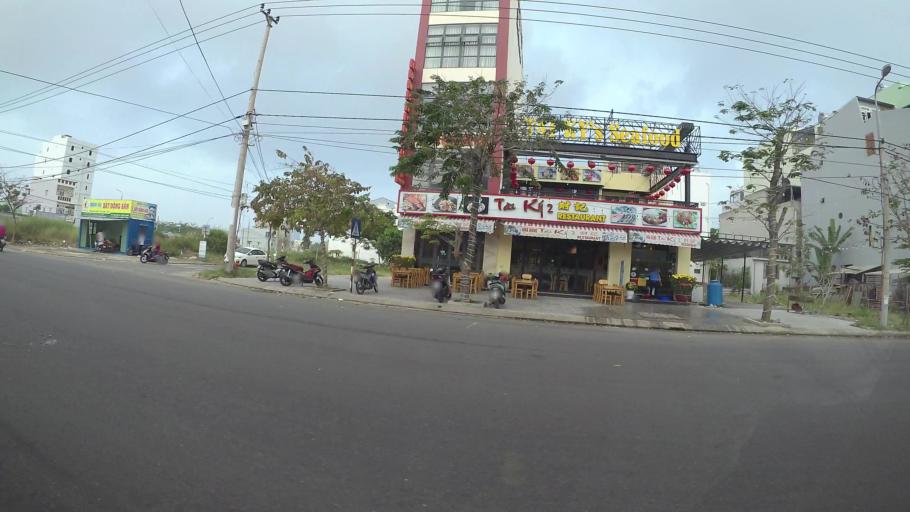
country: VN
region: Da Nang
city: Son Tra
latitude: 16.0814
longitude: 108.2440
